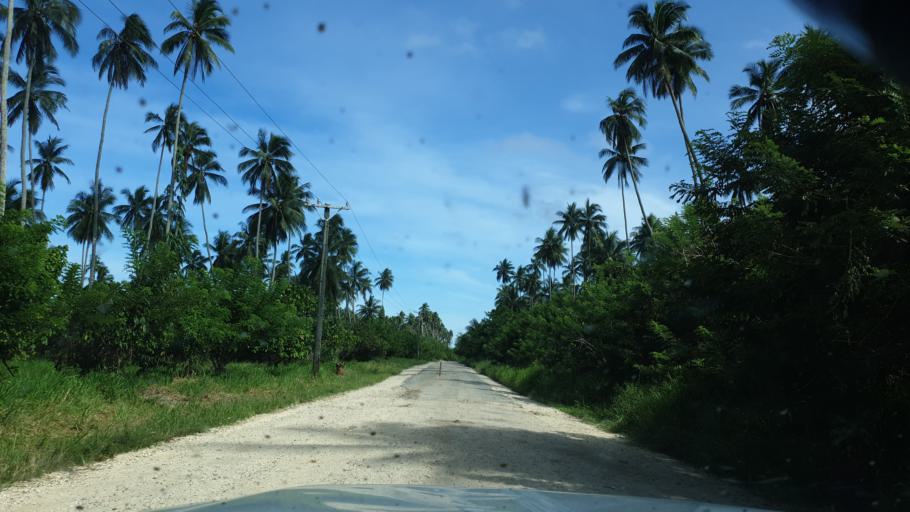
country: PG
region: Madang
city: Madang
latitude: -4.7780
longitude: 145.7071
